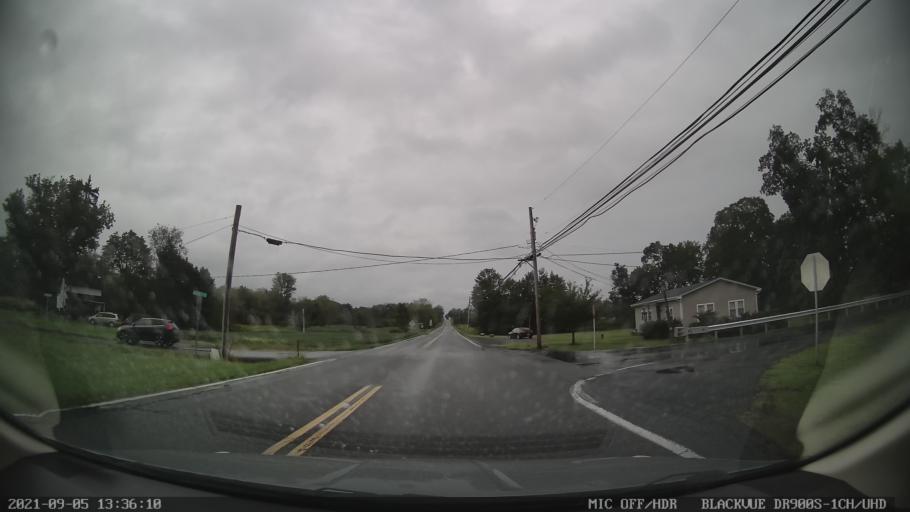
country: US
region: Pennsylvania
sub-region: Lehigh County
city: Breinigsville
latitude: 40.5775
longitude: -75.6608
